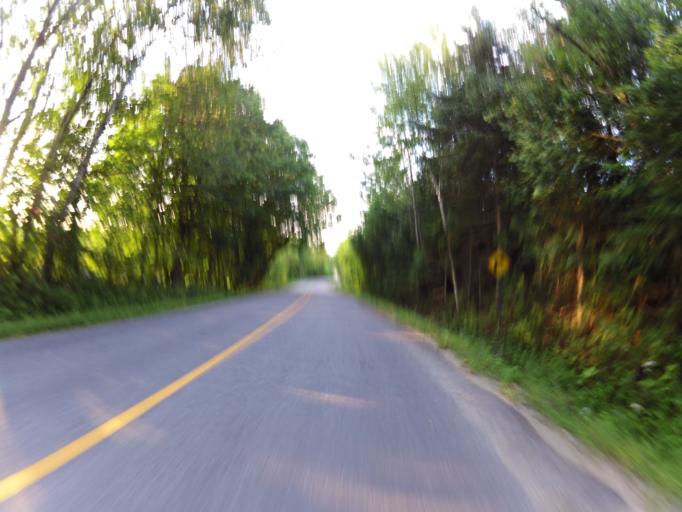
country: CA
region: Quebec
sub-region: Outaouais
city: Wakefield
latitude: 45.7290
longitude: -75.9712
